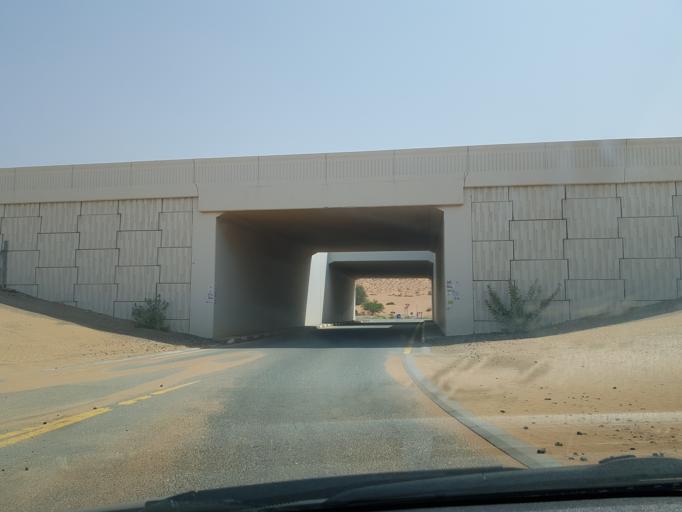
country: AE
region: Ra's al Khaymah
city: Ras al-Khaimah
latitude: 25.6194
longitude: 55.8004
